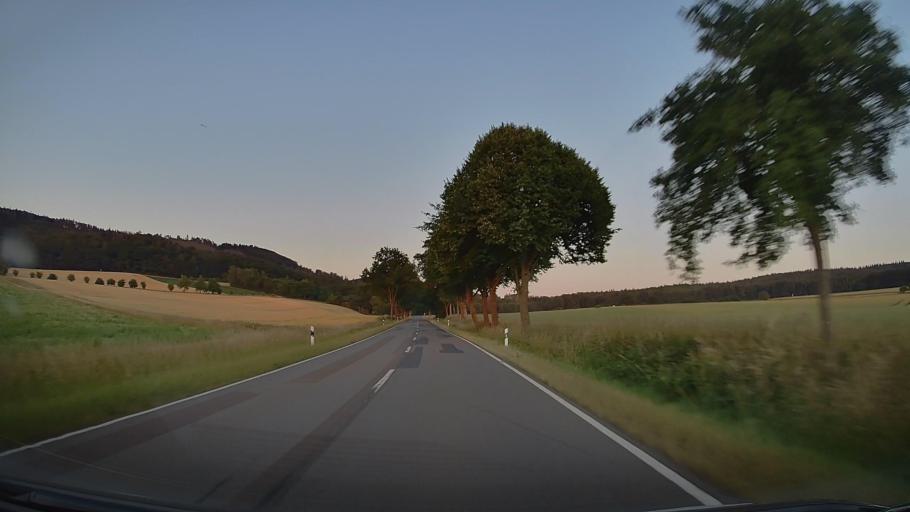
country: DE
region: Lower Saxony
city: Aerzen
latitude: 52.0322
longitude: 9.2698
